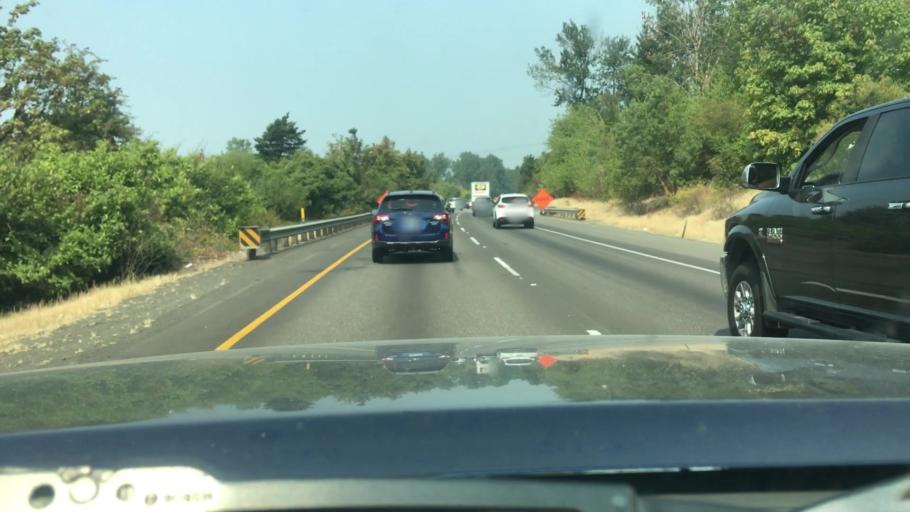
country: US
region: Oregon
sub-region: Clackamas County
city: West Linn
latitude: 45.3507
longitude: -122.6592
